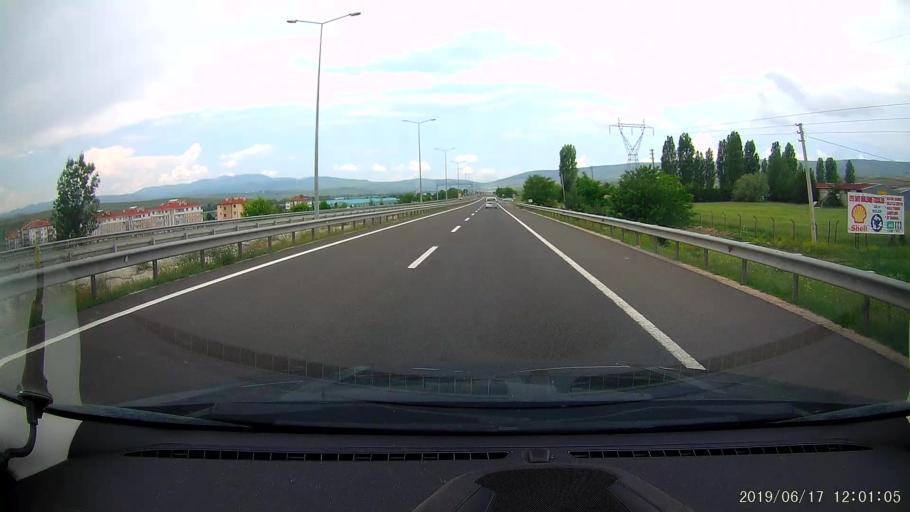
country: TR
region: Cankiri
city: Cerkes
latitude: 40.8204
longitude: 32.8766
